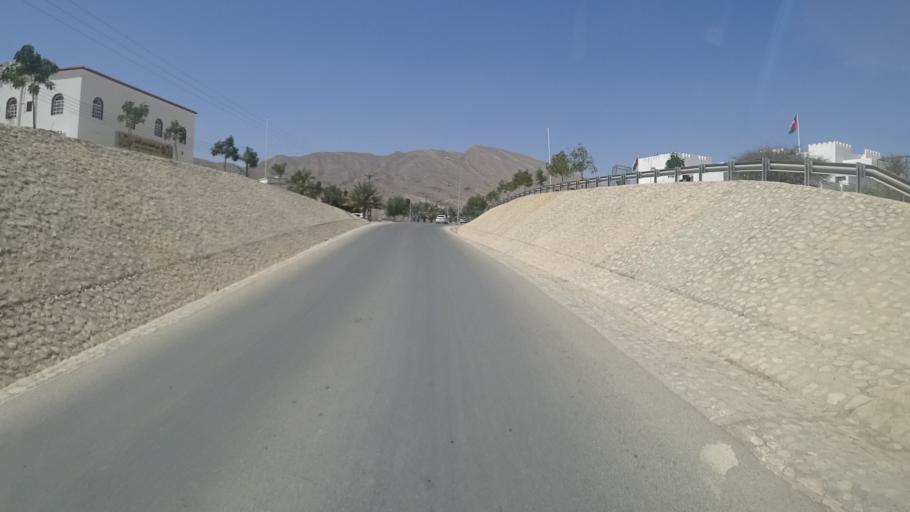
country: OM
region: Ash Sharqiyah
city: Badiyah
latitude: 22.5793
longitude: 59.0941
